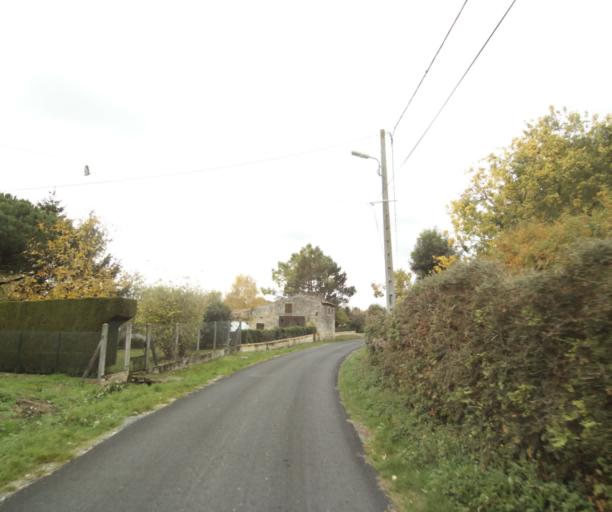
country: FR
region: Poitou-Charentes
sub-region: Departement de la Charente-Maritime
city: Saint-Georges-des-Coteaux
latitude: 45.7800
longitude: -0.6946
